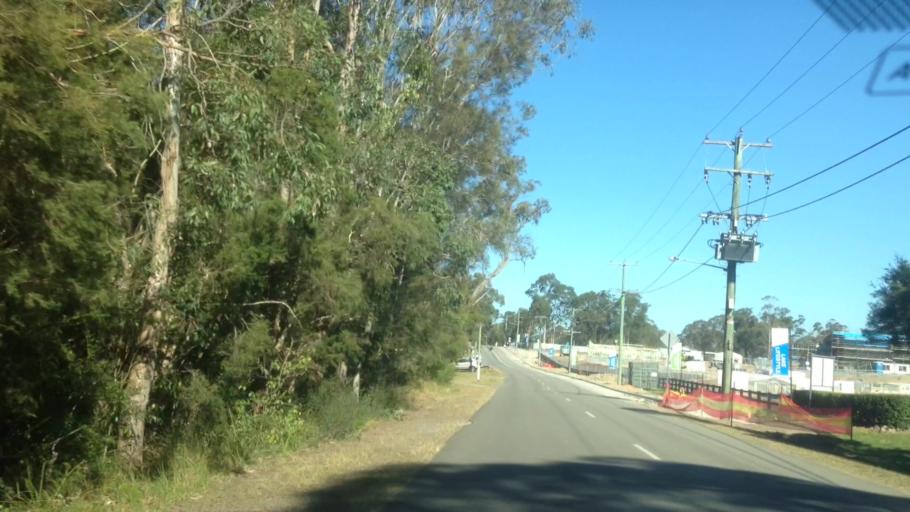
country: AU
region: New South Wales
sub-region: Lake Macquarie Shire
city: Cooranbong
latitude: -33.0903
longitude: 151.4501
